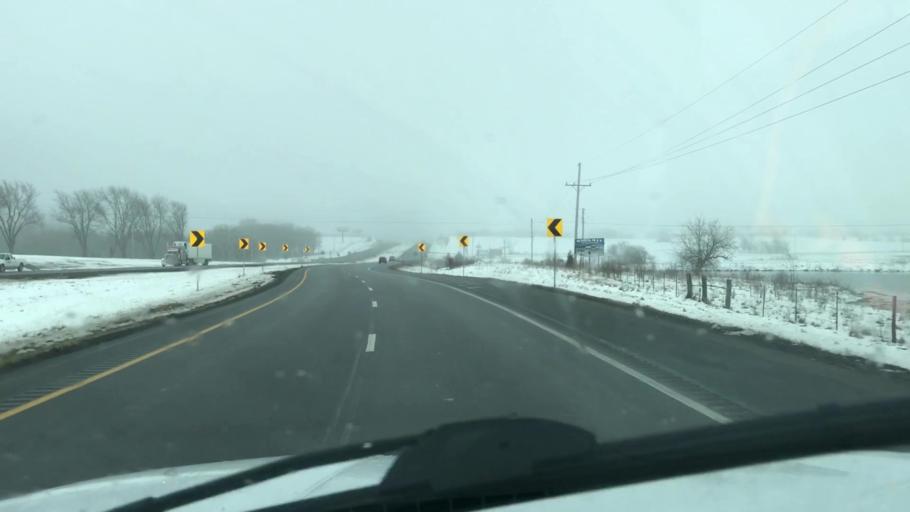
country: US
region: Missouri
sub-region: Clinton County
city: Cameron
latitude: 39.7538
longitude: -94.2686
